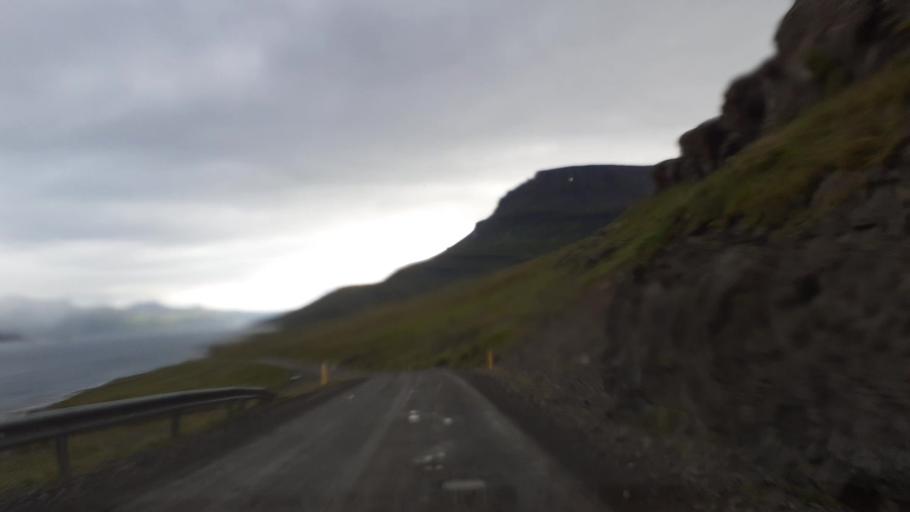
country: IS
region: East
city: Reydarfjoerdur
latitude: 65.0125
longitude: -14.1803
